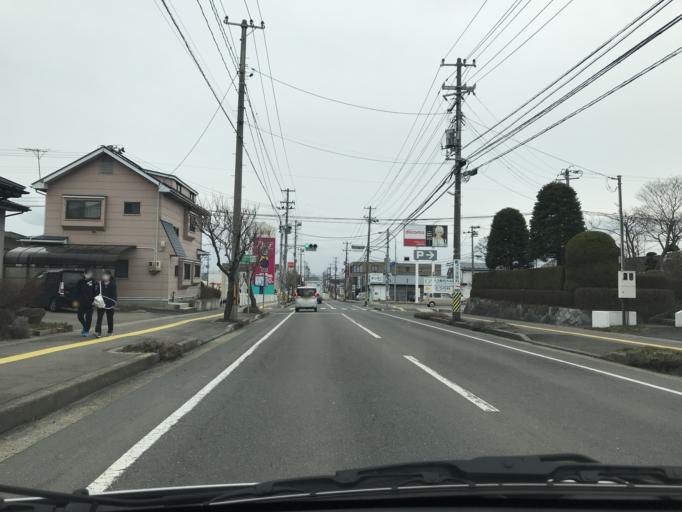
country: JP
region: Iwate
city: Hanamaki
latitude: 39.3987
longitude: 141.1062
